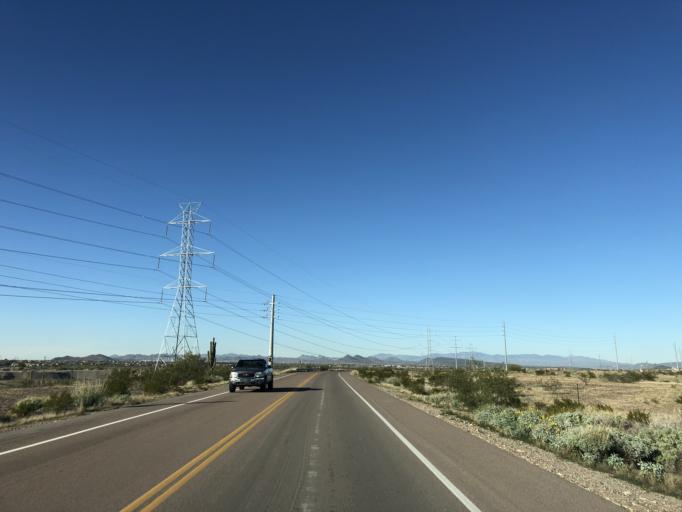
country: US
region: Arizona
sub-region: Maricopa County
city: Sun City West
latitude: 33.6762
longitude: -112.2995
